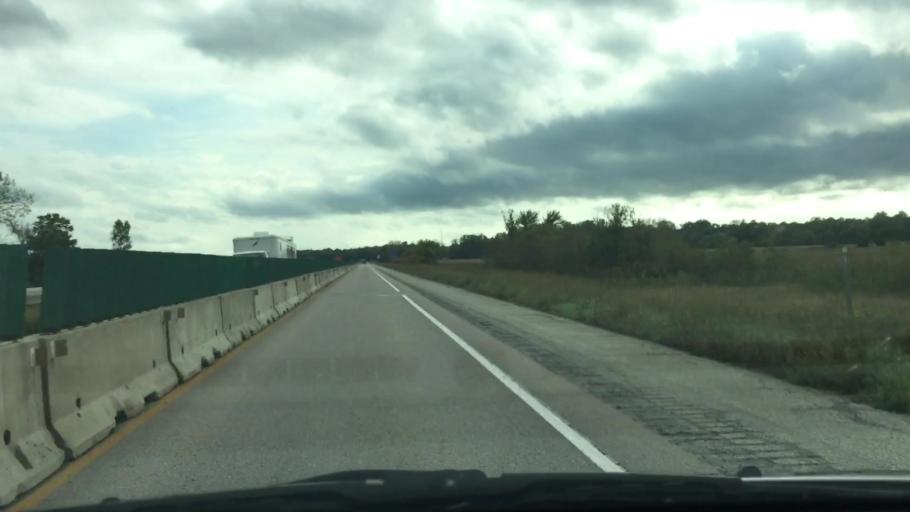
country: US
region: Iowa
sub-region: Decatur County
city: Lamoni
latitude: 40.6762
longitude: -93.8493
